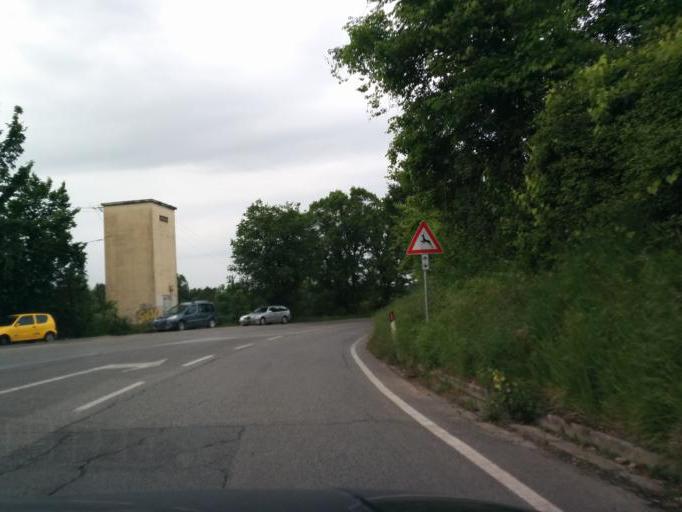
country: IT
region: Tuscany
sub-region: Province of Florence
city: San Casciano in Val di Pesa
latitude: 43.6285
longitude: 11.1825
